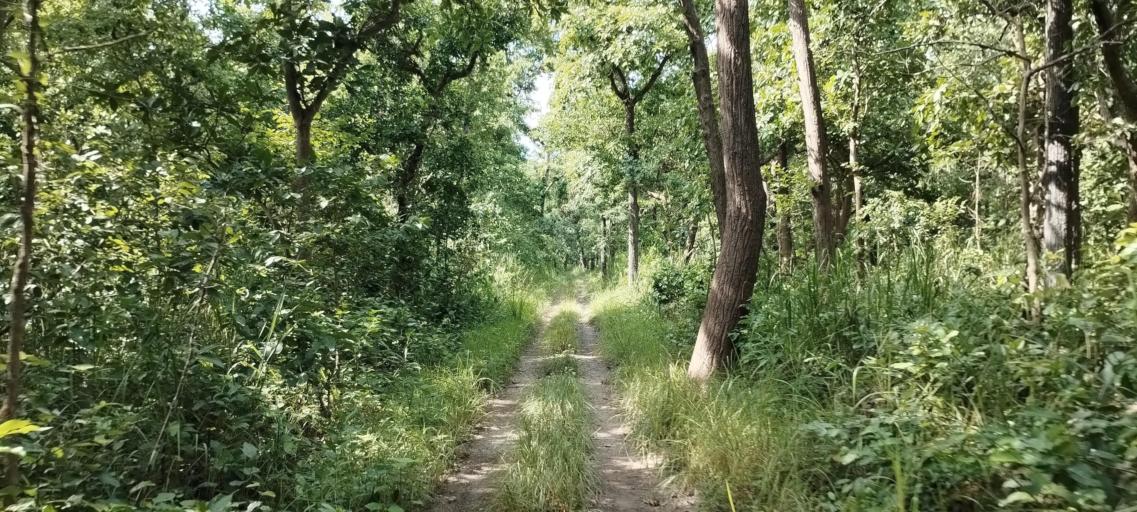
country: NP
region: Far Western
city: Tikapur
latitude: 28.5626
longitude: 81.2943
